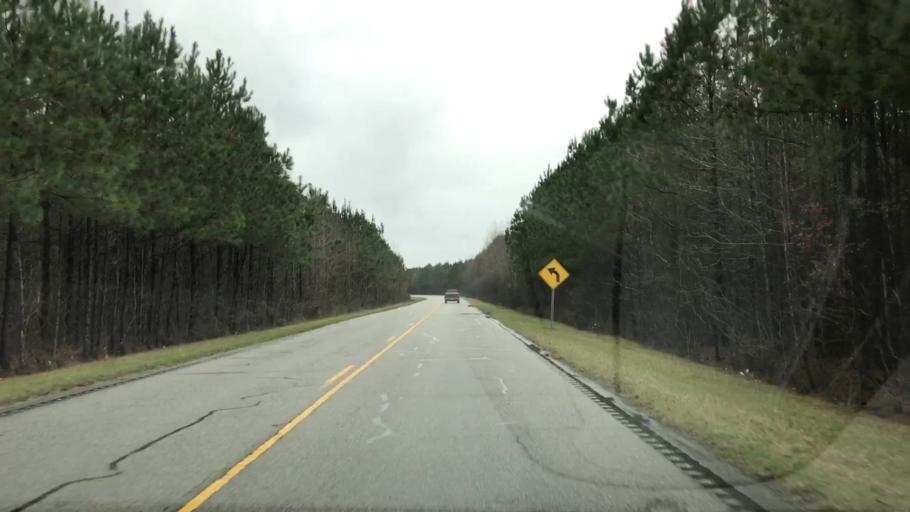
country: US
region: South Carolina
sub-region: Williamsburg County
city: Andrews
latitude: 33.5385
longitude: -79.4813
